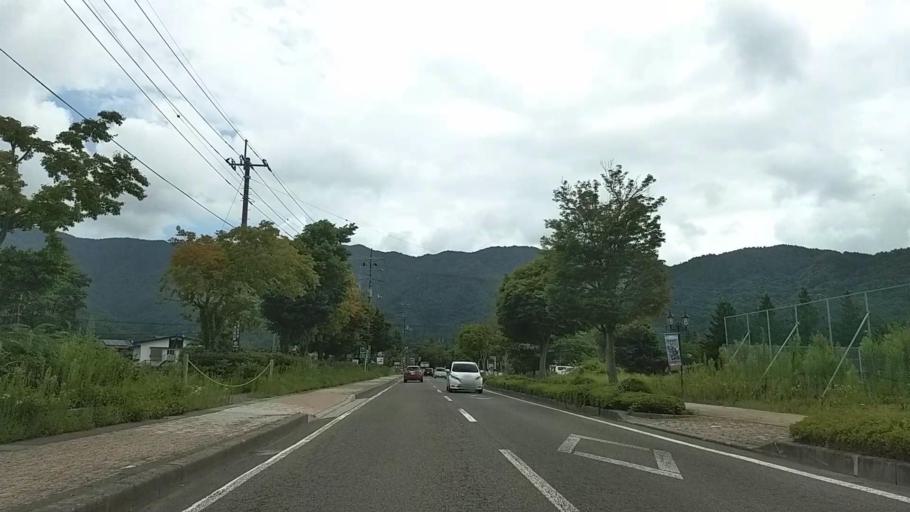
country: JP
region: Yamanashi
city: Fujikawaguchiko
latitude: 35.5239
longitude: 138.7669
